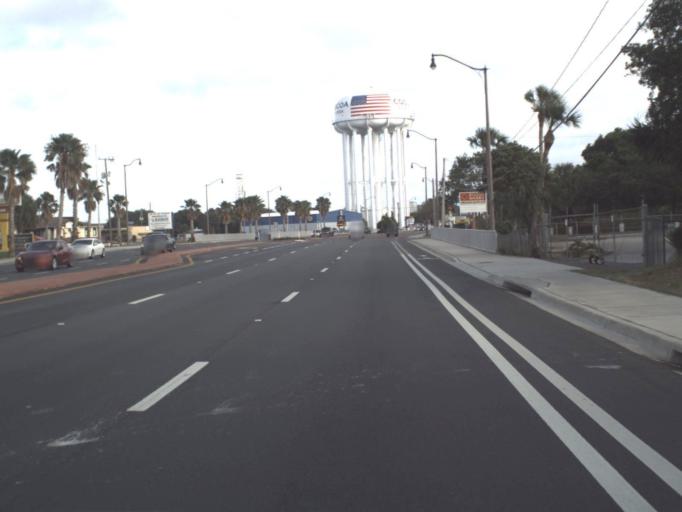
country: US
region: Florida
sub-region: Brevard County
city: Rockledge
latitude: 28.3609
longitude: -80.7336
